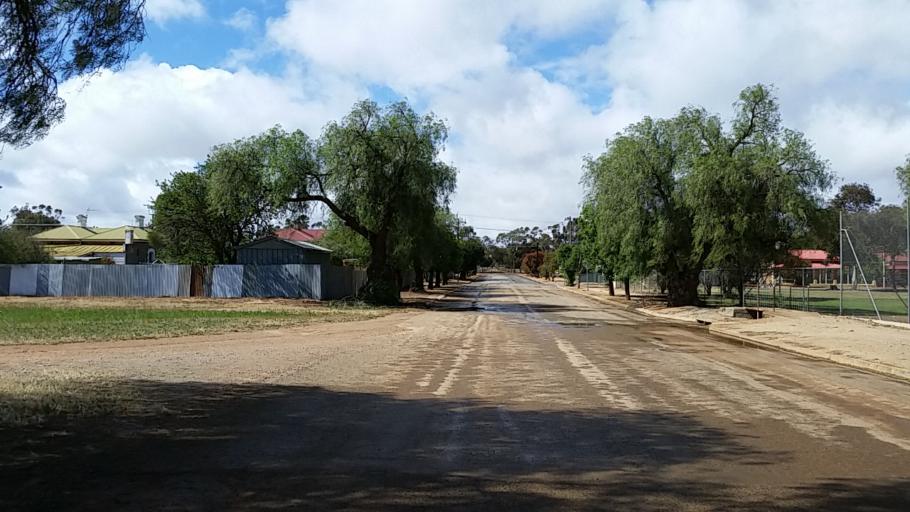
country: AU
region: South Australia
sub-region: Peterborough
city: Peterborough
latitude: -32.9718
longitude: 138.8332
